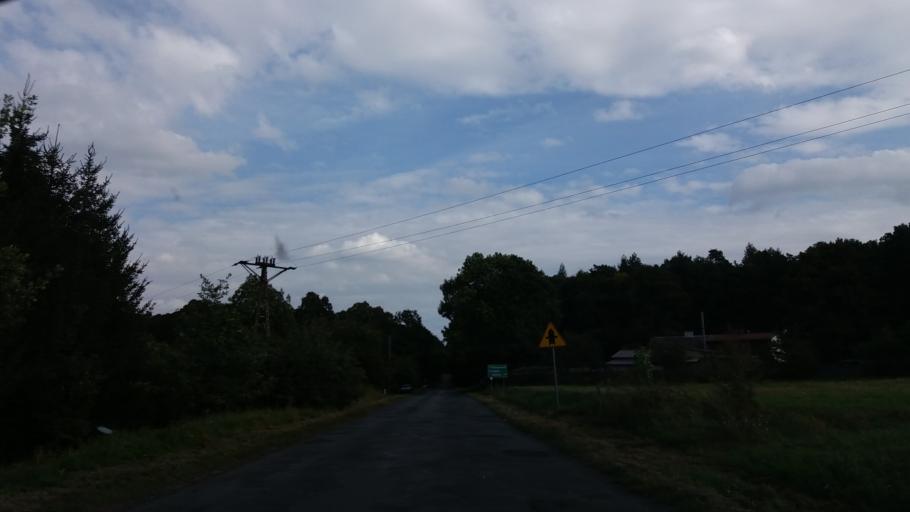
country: PL
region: West Pomeranian Voivodeship
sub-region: Powiat stargardzki
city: Dolice
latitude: 53.2412
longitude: 15.2366
